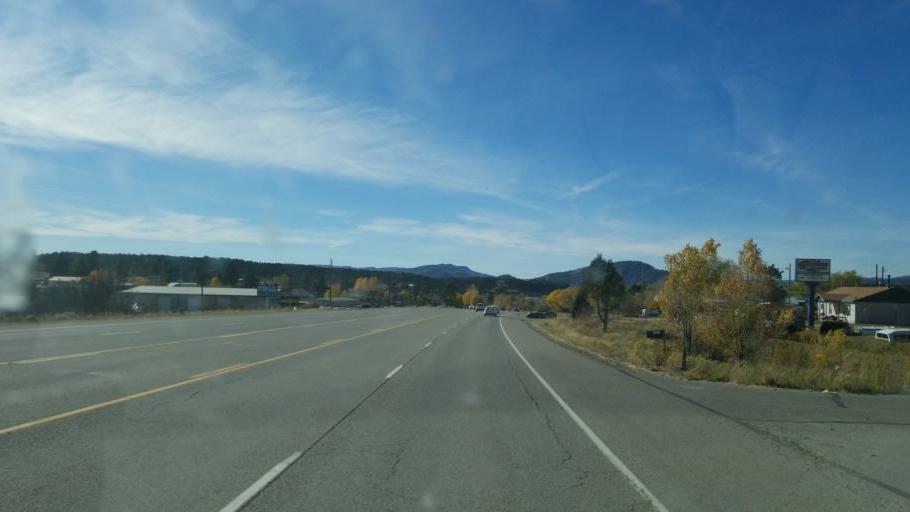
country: US
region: Colorado
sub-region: La Plata County
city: Durango
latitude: 37.2273
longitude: -107.8115
